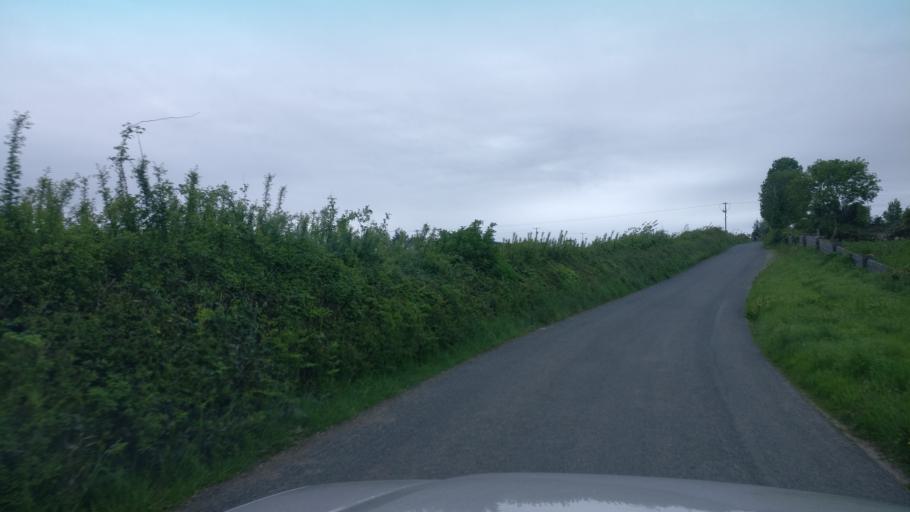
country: IE
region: Connaught
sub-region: County Galway
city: Loughrea
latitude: 53.1189
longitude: -8.4286
